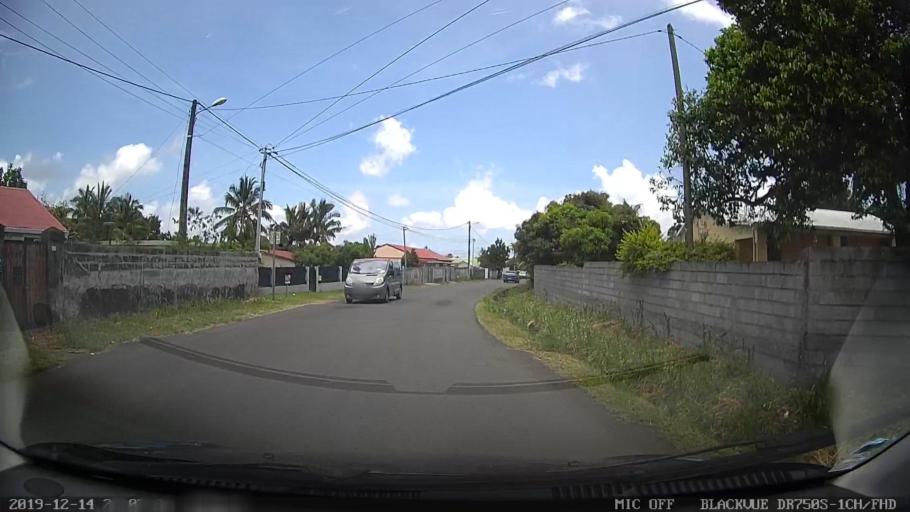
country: RE
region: Reunion
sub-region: Reunion
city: Saint-Andre
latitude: -20.9478
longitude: 55.6627
